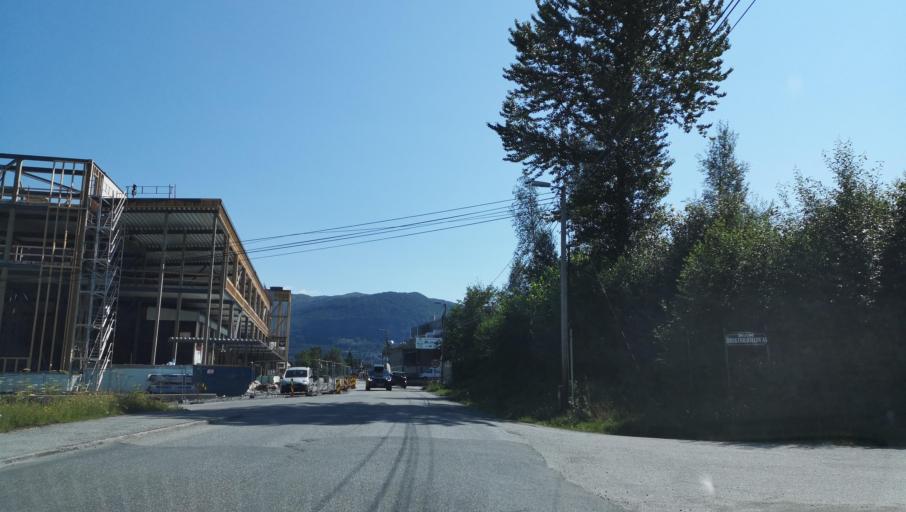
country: NO
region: Hordaland
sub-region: Voss
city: Voss
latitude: 60.6348
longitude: 6.4582
